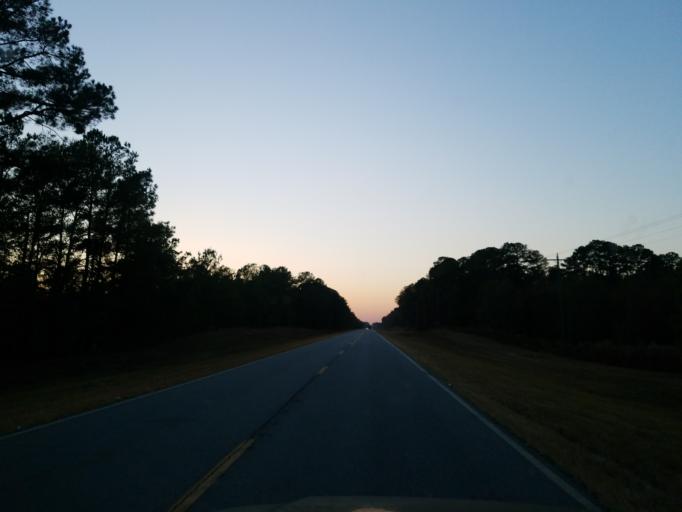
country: US
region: Georgia
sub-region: Turner County
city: Ashburn
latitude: 31.7213
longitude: -83.4791
